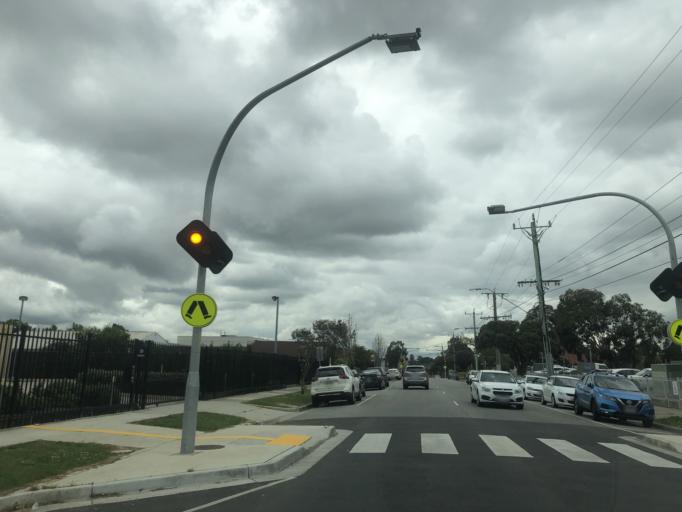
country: AU
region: Victoria
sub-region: Greater Dandenong
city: Dandenong North
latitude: -37.9749
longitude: 145.2164
